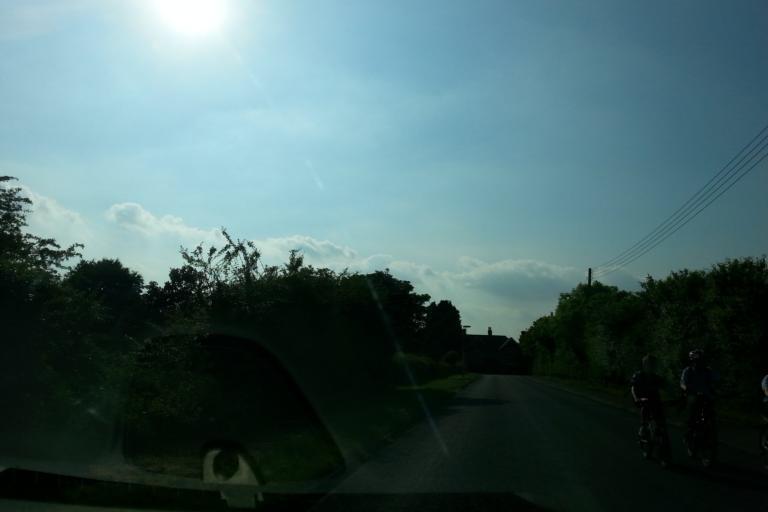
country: GB
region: England
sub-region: Cambridgeshire
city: Swavesey
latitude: 52.3126
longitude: 0.0090
